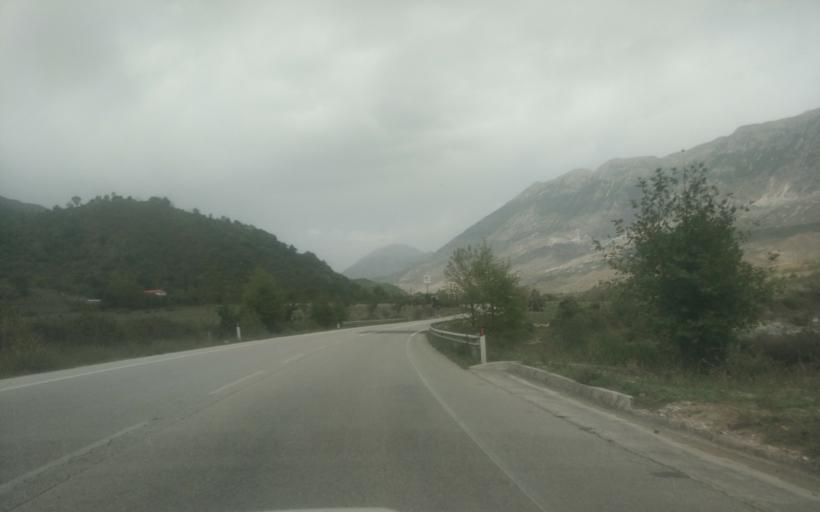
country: AL
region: Gjirokaster
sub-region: Rrethi i Gjirokastres
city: Picar
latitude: 40.2063
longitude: 20.0890
